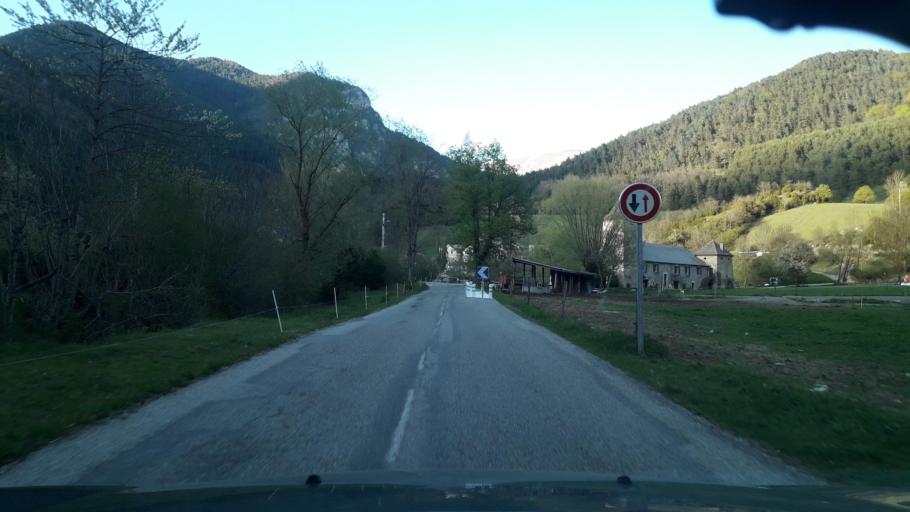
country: FR
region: Rhone-Alpes
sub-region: Departement de l'Isere
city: Mens
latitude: 44.6851
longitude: 5.5951
